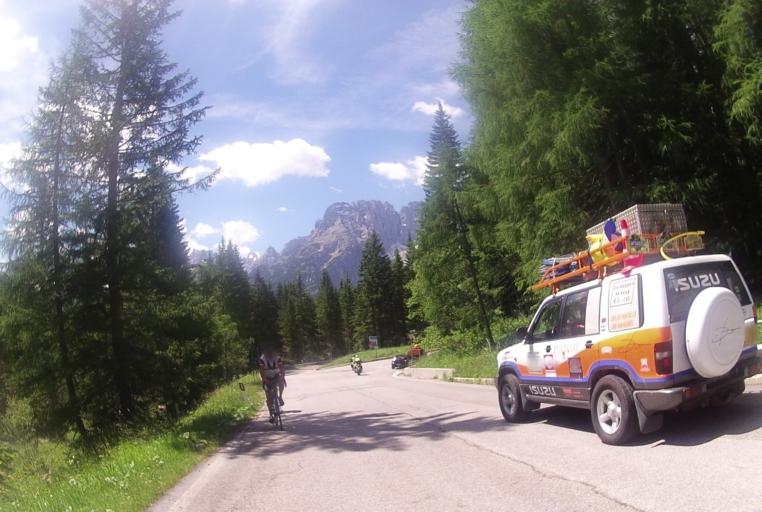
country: IT
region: Veneto
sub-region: Provincia di Belluno
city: Cortina d'Ampezzo
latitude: 46.5660
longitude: 12.2444
